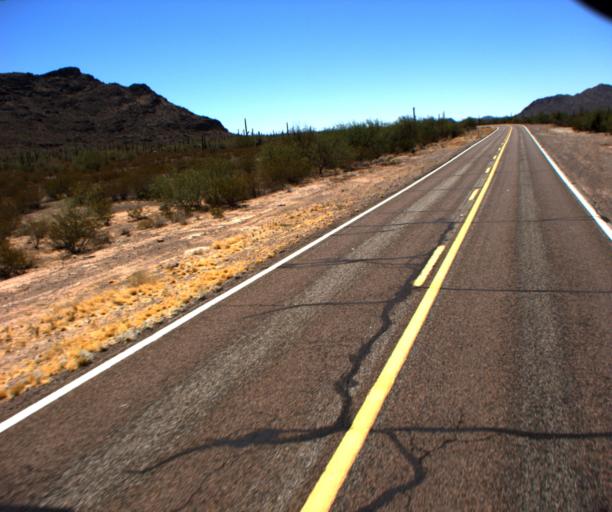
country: US
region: Arizona
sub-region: Pima County
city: Ajo
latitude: 32.2304
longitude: -112.7120
